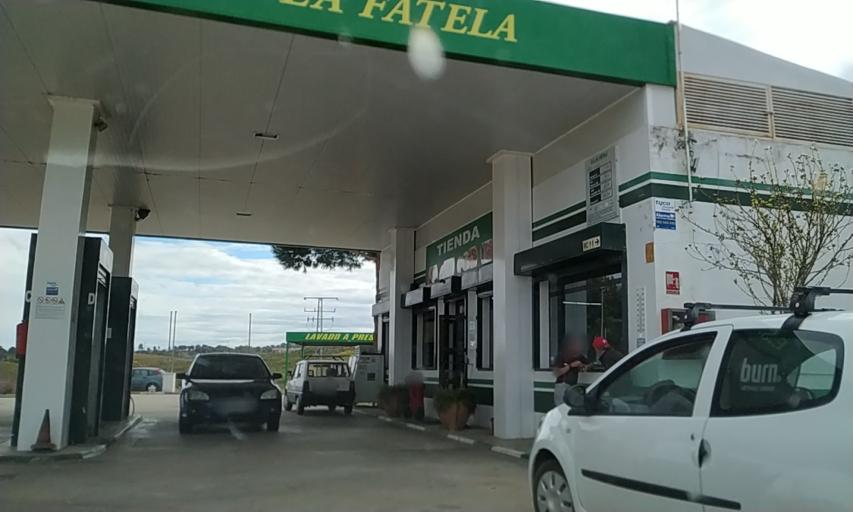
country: ES
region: Extremadura
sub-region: Provincia de Caceres
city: Perales del Puerto
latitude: 40.1732
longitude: -6.6763
